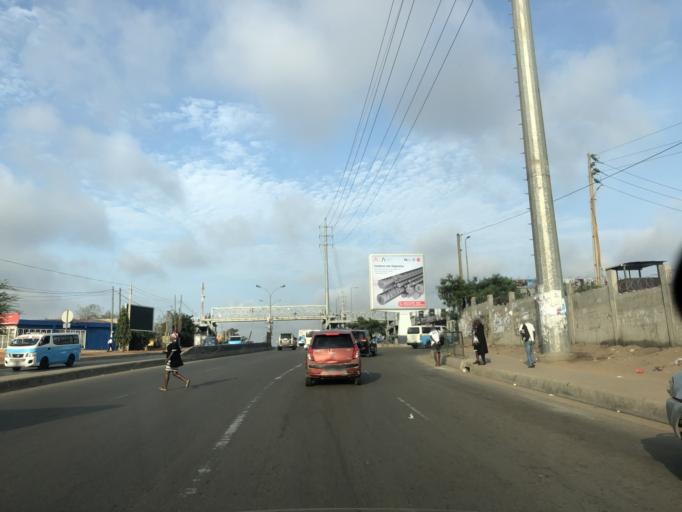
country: AO
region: Luanda
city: Luanda
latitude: -8.8981
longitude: 13.2160
